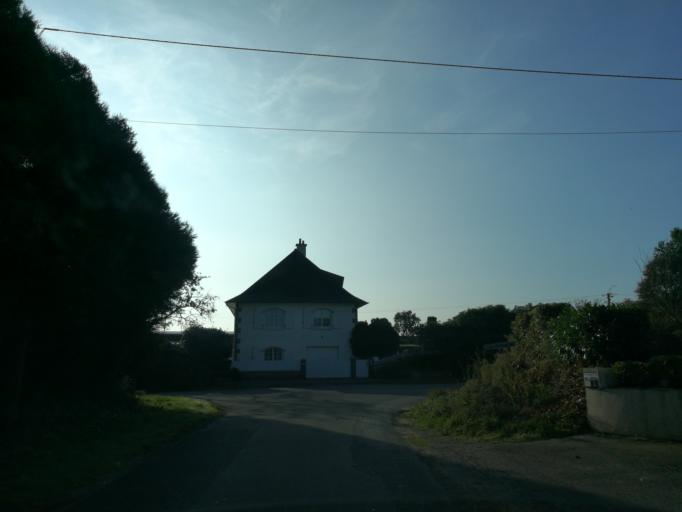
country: FR
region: Brittany
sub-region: Departement d'Ille-et-Vilaine
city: Pleumeleuc
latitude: 48.1727
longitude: -1.9132
